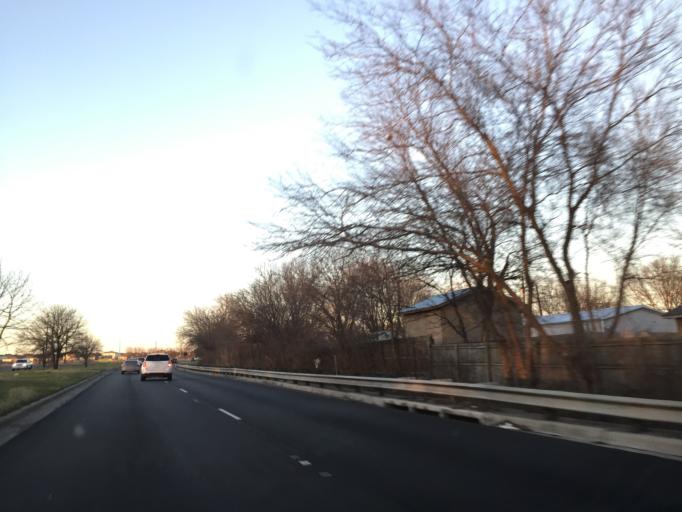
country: US
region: Texas
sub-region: Travis County
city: Pflugerville
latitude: 30.4090
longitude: -97.6352
